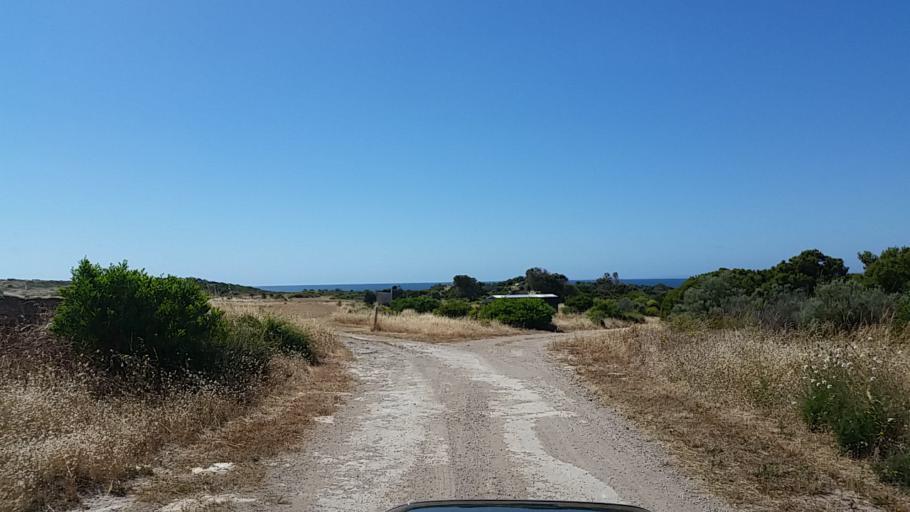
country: AU
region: South Australia
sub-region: Yorke Peninsula
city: Honiton
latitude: -35.2352
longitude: 137.1161
